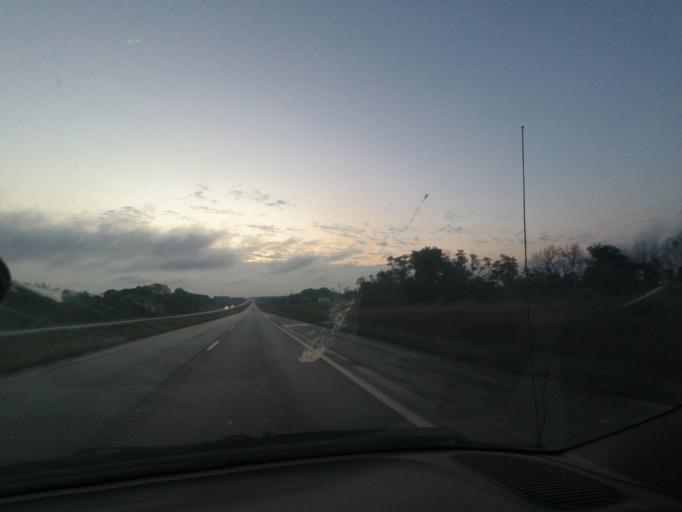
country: US
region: Missouri
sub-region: Linn County
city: Marceline
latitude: 39.7621
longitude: -93.0024
